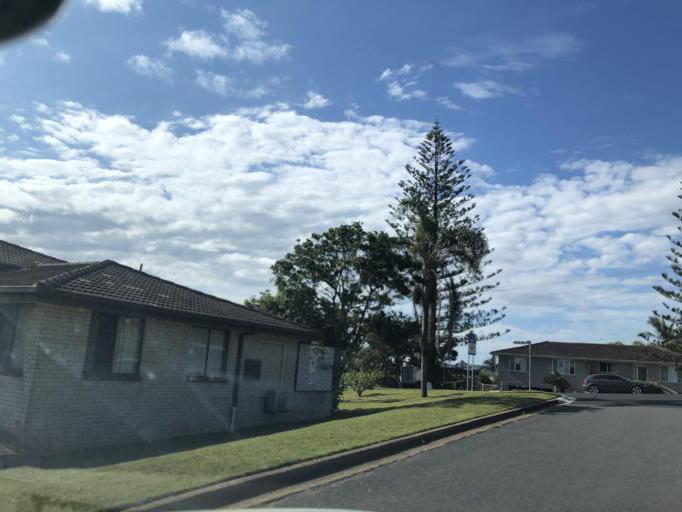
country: AU
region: New South Wales
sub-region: Coffs Harbour
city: Moonee Beach
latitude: -30.2344
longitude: 153.1514
